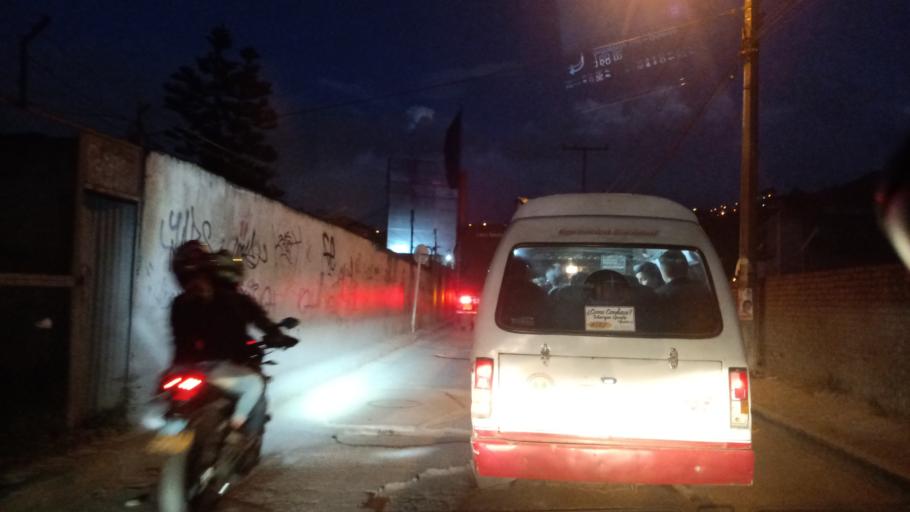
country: CO
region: Cundinamarca
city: Soacha
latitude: 4.5677
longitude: -74.2289
